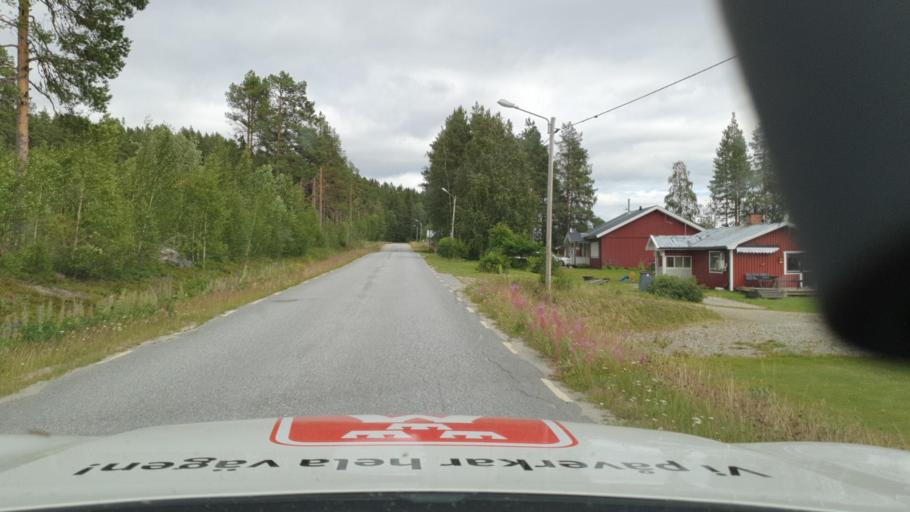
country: SE
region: Vaesterbotten
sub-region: Dorotea Kommun
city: Dorotea
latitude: 64.1904
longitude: 16.6324
